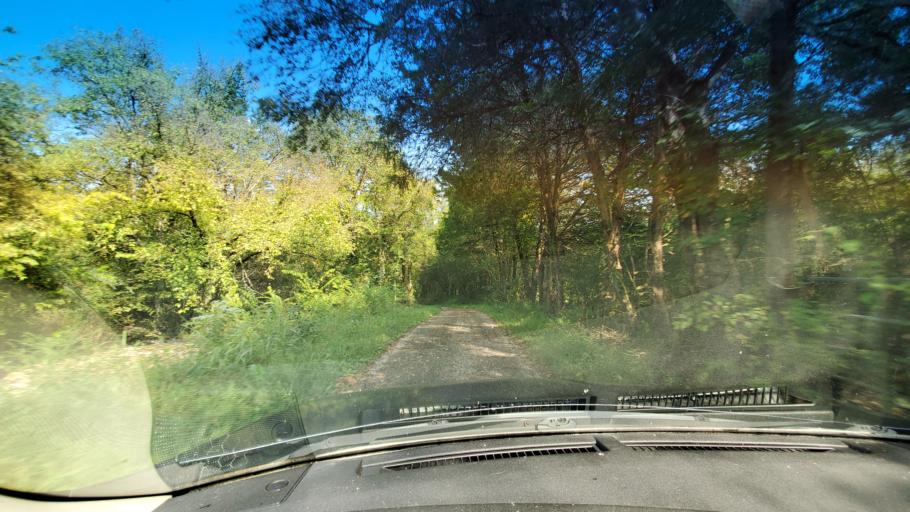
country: US
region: Tennessee
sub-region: Smith County
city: South Carthage
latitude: 36.2308
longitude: -85.9835
